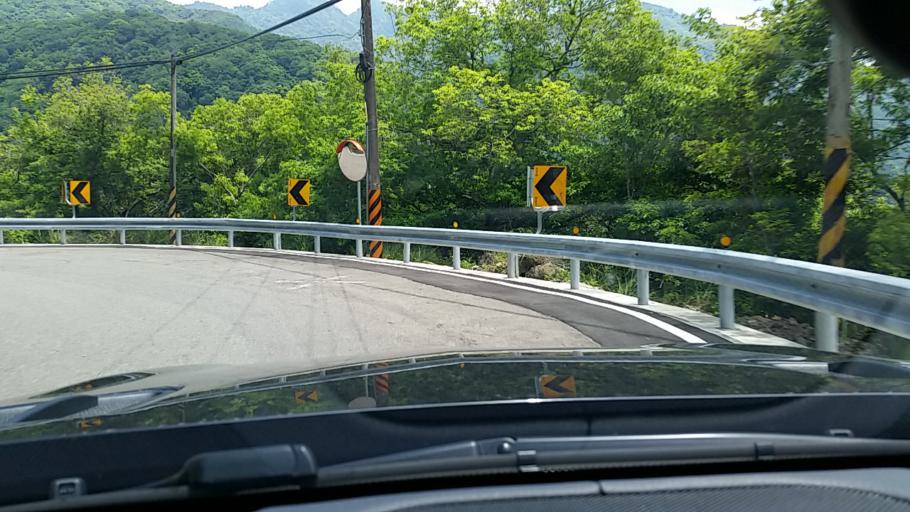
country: TW
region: Taiwan
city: Daxi
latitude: 24.7024
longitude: 121.3640
